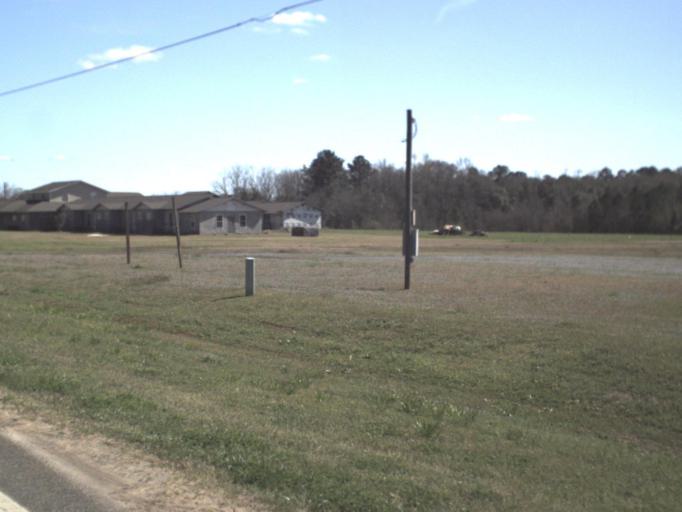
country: US
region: Florida
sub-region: Gadsden County
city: Quincy
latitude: 30.5865
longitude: -84.6191
